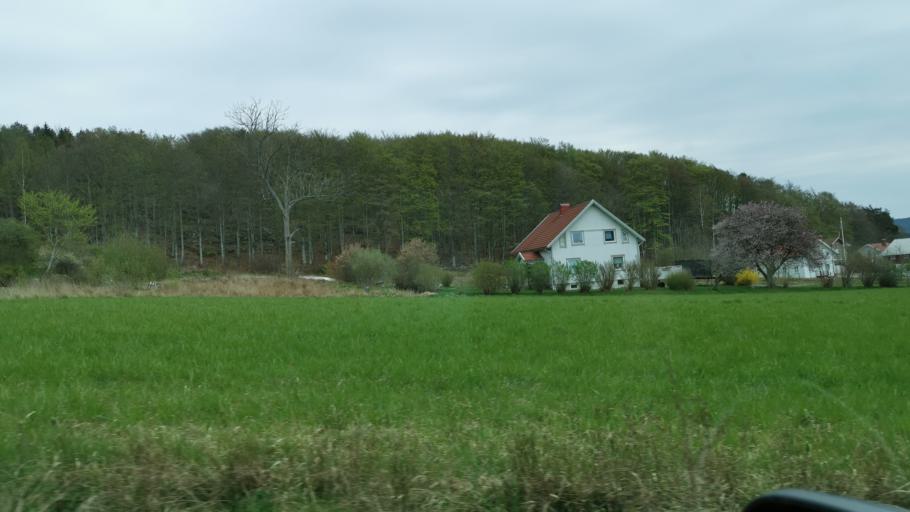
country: SE
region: Vaestra Goetaland
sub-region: Orust
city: Henan
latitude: 58.2778
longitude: 11.6401
